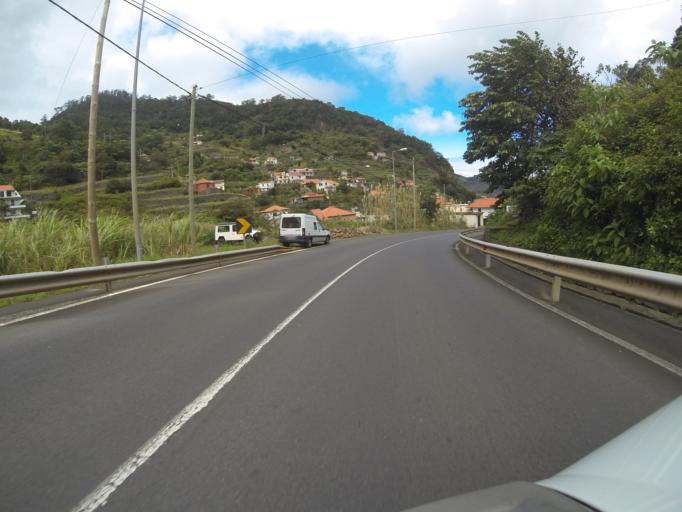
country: PT
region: Madeira
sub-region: Machico
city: Machico
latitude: 32.7338
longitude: -16.7862
